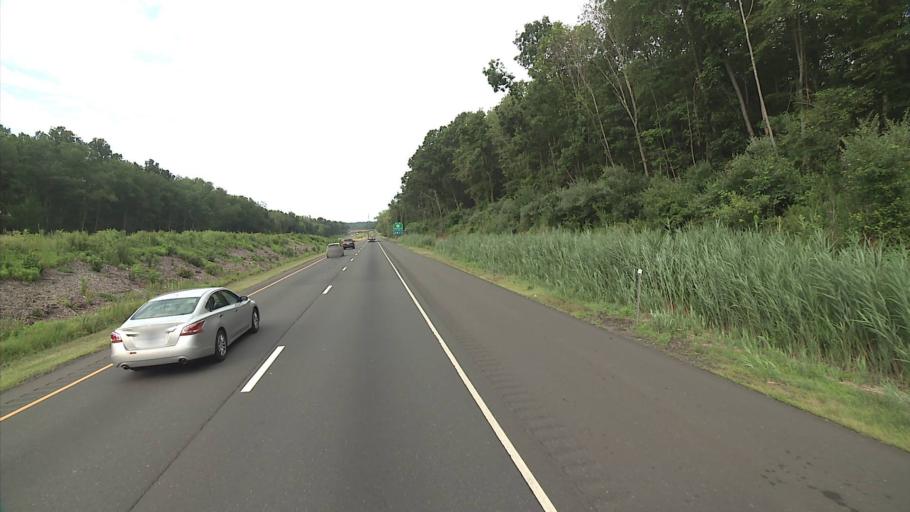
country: US
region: Connecticut
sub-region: New Haven County
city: Middlebury
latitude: 41.5063
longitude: -73.1437
